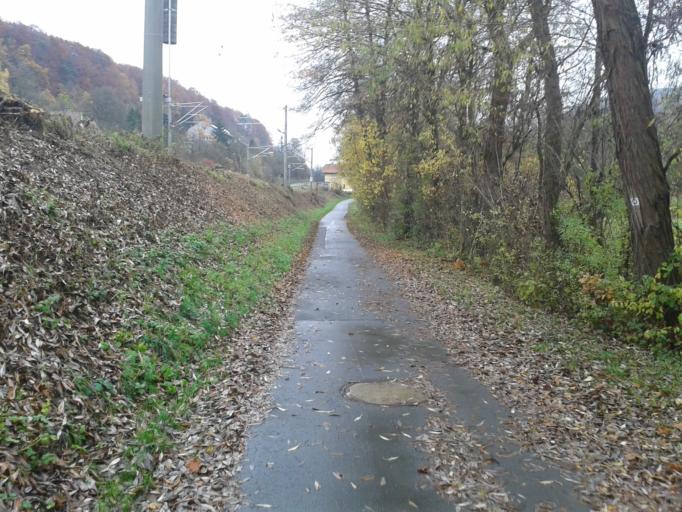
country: DE
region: Bavaria
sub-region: Regierungsbezirk Mittelfranken
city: Pommelsbrunn
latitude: 49.5012
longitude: 11.5152
